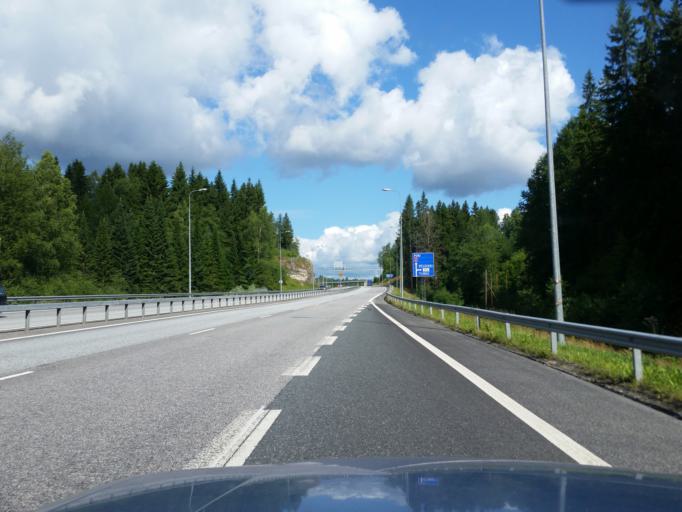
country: FI
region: Uusimaa
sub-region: Helsinki
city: Vihti
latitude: 60.2972
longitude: 24.3621
